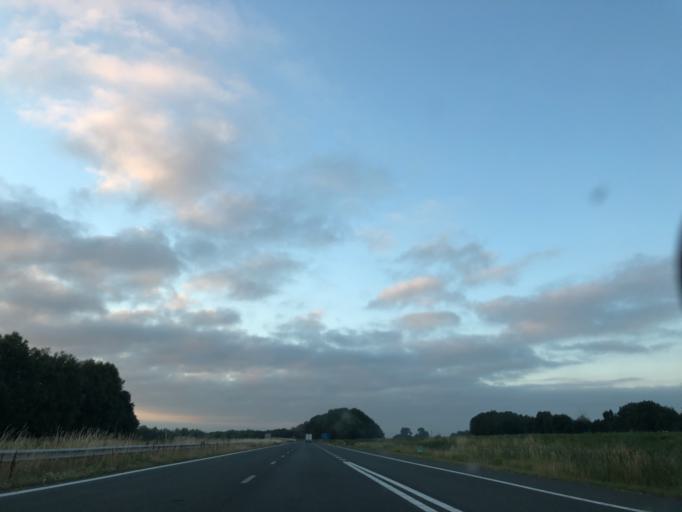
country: NL
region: Groningen
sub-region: Gemeente  Oldambt
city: Winschoten
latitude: 53.1530
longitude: 7.0606
